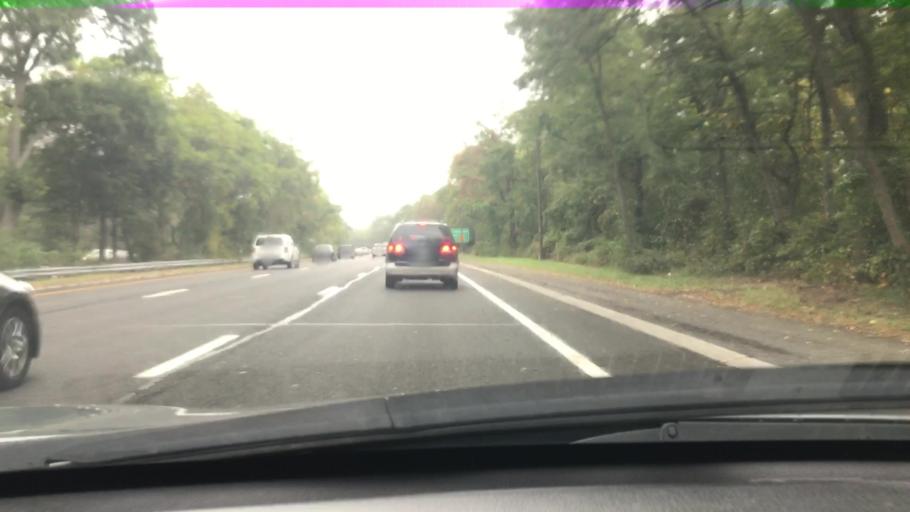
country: US
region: New York
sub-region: Suffolk County
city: North Amityville
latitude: 40.7051
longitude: -73.4386
